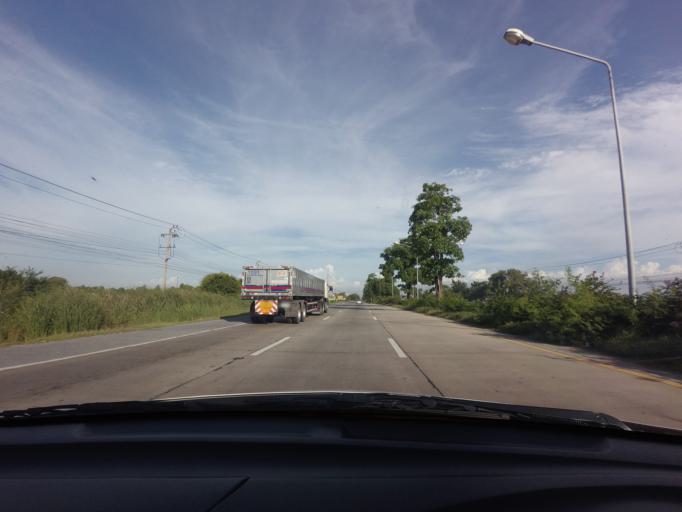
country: TH
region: Phra Nakhon Si Ayutthaya
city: Lat Bua Luang
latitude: 14.0819
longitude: 100.3140
